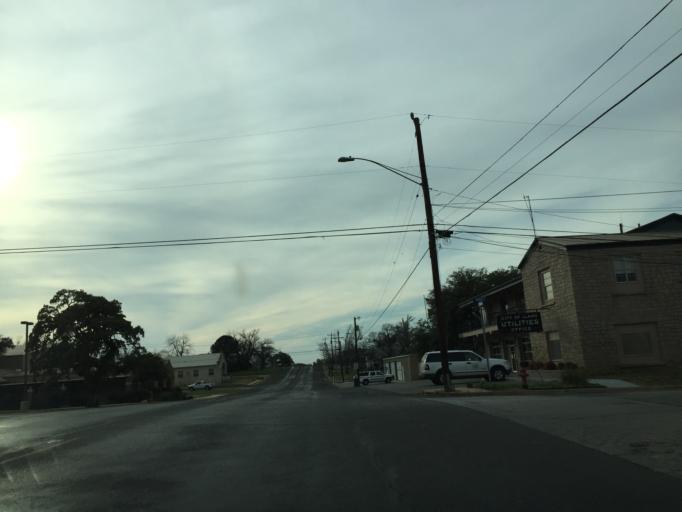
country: US
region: Texas
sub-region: Llano County
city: Llano
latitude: 30.7504
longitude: -98.6781
